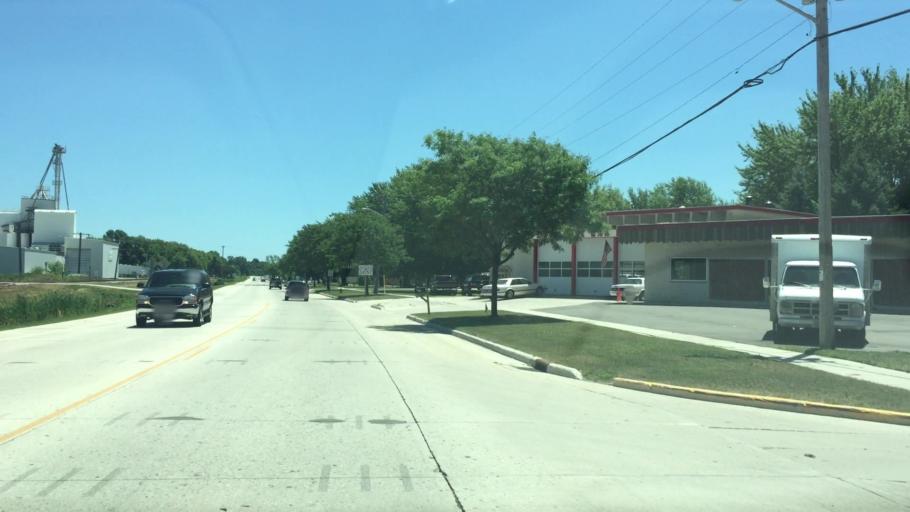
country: US
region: Wisconsin
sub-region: Calumet County
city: New Holstein
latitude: 43.9480
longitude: -88.0823
